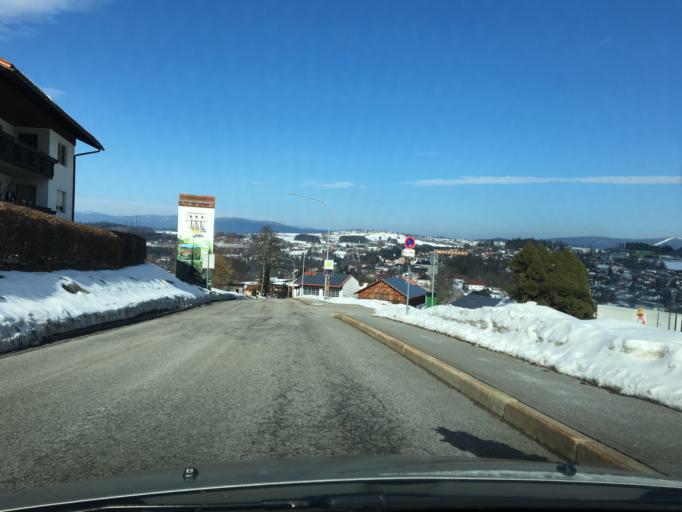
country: DE
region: Bavaria
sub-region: Lower Bavaria
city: Freyung
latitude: 48.7978
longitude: 13.5429
